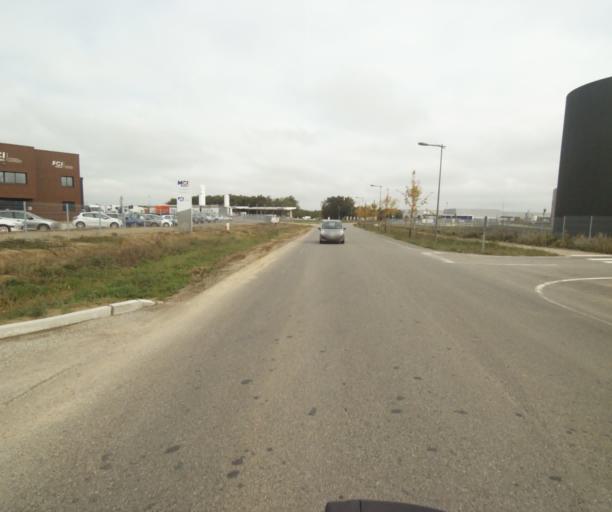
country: FR
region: Midi-Pyrenees
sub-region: Departement du Tarn-et-Garonne
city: Campsas
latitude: 43.9132
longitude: 1.3080
